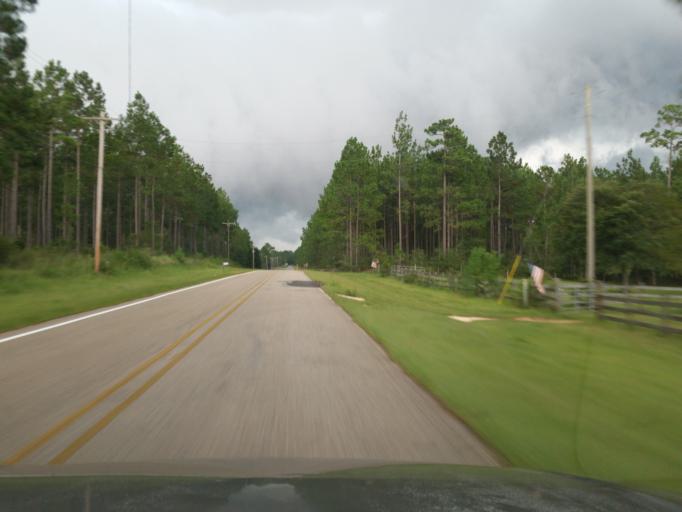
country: US
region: Alabama
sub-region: Baldwin County
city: Robertsdale
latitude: 30.5863
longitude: -87.5630
